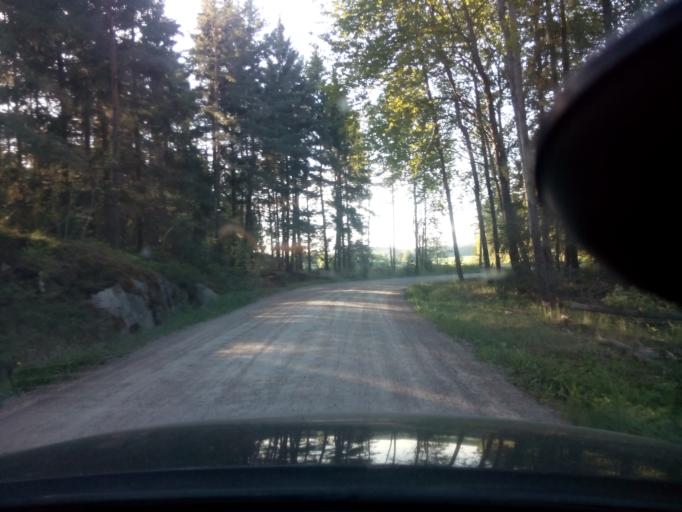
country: SE
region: Soedermanland
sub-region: Nykopings Kommun
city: Nykoping
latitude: 58.7795
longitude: 17.0472
